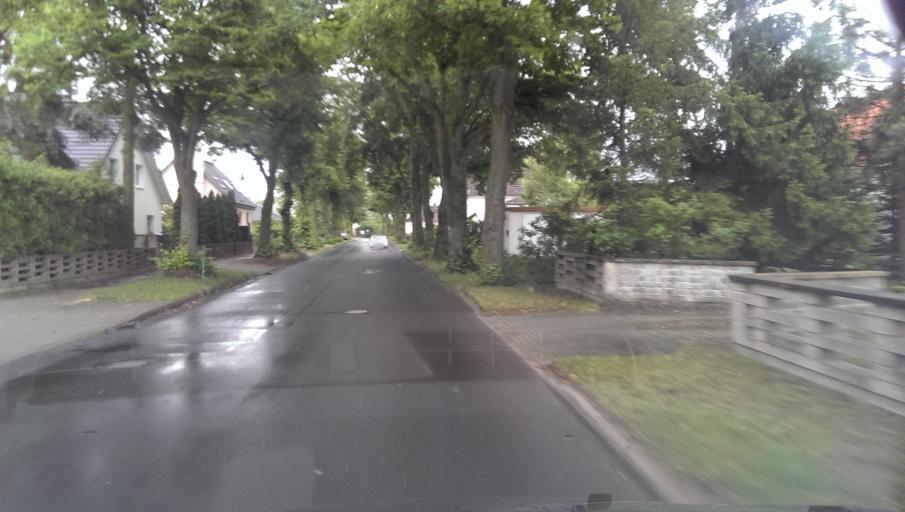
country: DE
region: Brandenburg
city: Gross Kreutz
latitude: 52.3613
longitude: 12.7504
